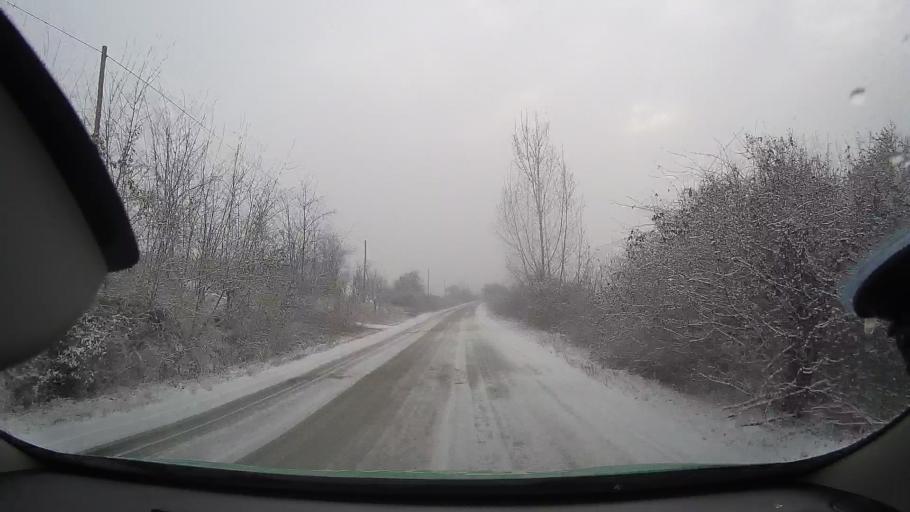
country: RO
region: Alba
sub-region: Municipiul Aiud
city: Aiudul de Sus
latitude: 46.3313
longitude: 23.6747
